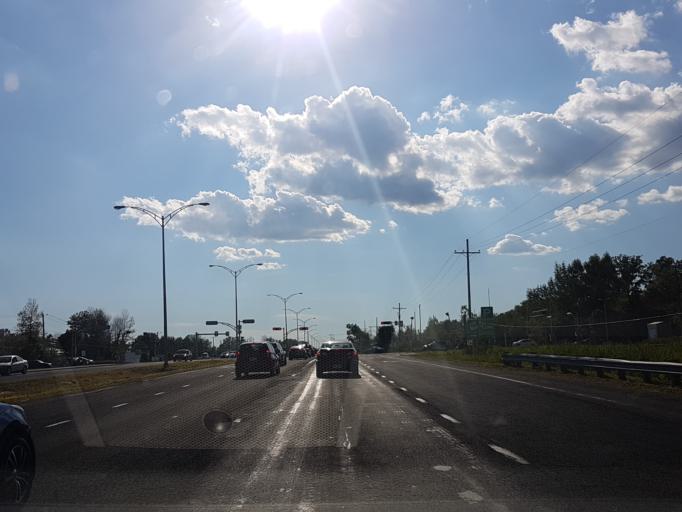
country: CA
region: Quebec
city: Saint-Bruno-de-Montarville
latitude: 45.5138
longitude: -73.3421
